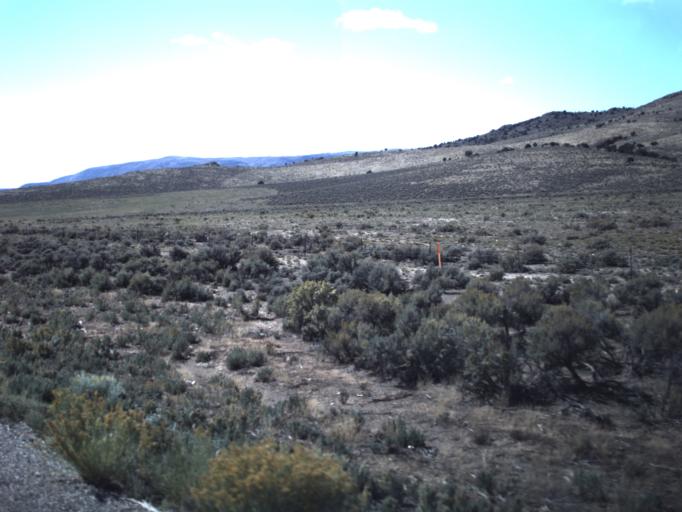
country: US
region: Utah
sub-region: Piute County
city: Junction
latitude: 38.3137
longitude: -111.9670
